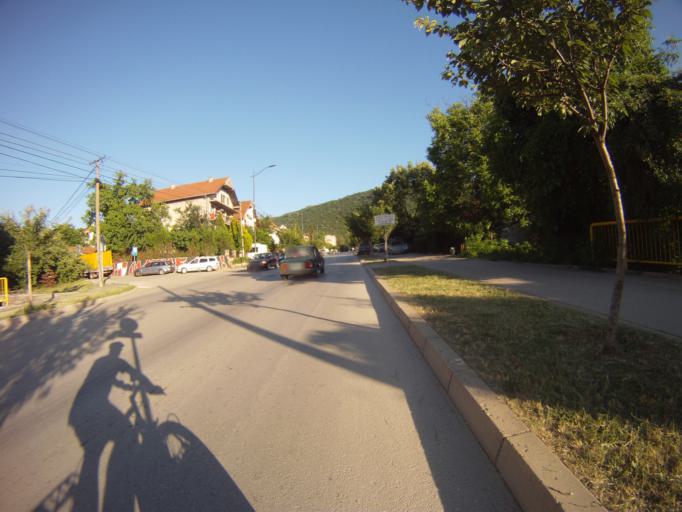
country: RS
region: Central Serbia
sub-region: Nisavski Okrug
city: Niska Banja
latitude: 43.2963
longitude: 22.0023
